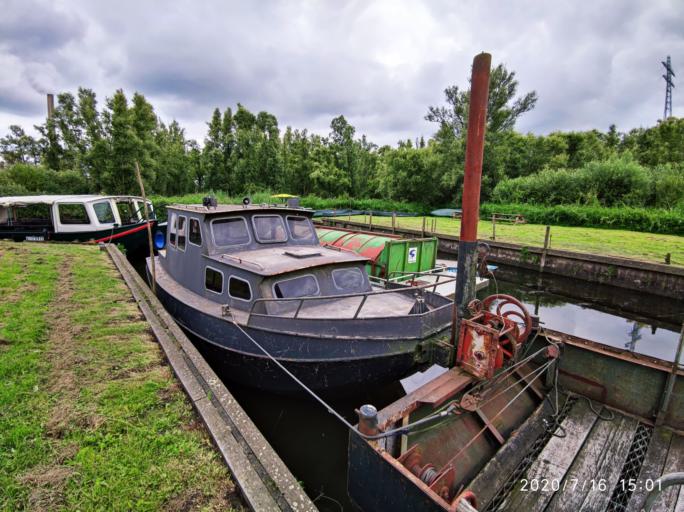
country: NL
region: North Brabant
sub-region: Gemeente Geertruidenberg
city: Geertruidenberg
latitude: 51.7170
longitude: 4.8366
